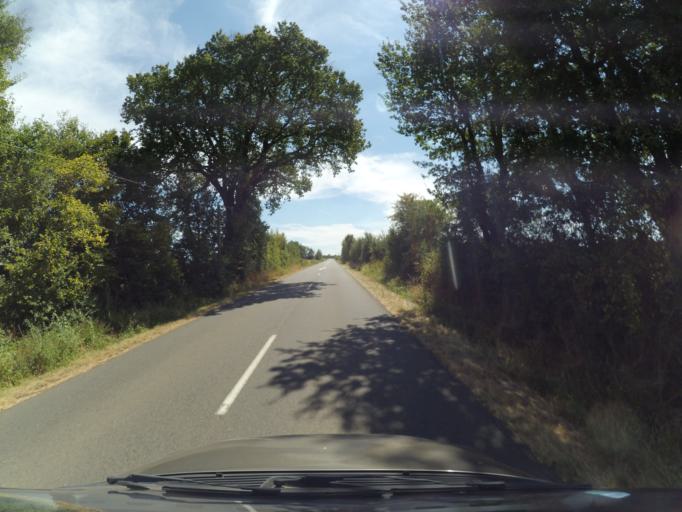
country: FR
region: Poitou-Charentes
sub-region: Departement de la Vienne
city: Usson-du-Poitou
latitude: 46.2595
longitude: 0.5226
